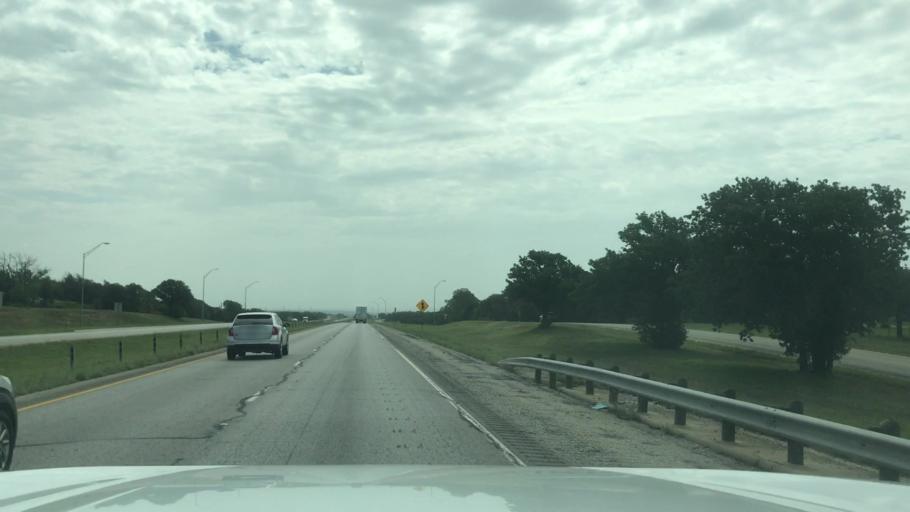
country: US
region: Texas
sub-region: Callahan County
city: Clyde
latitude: 32.4073
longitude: -99.4533
